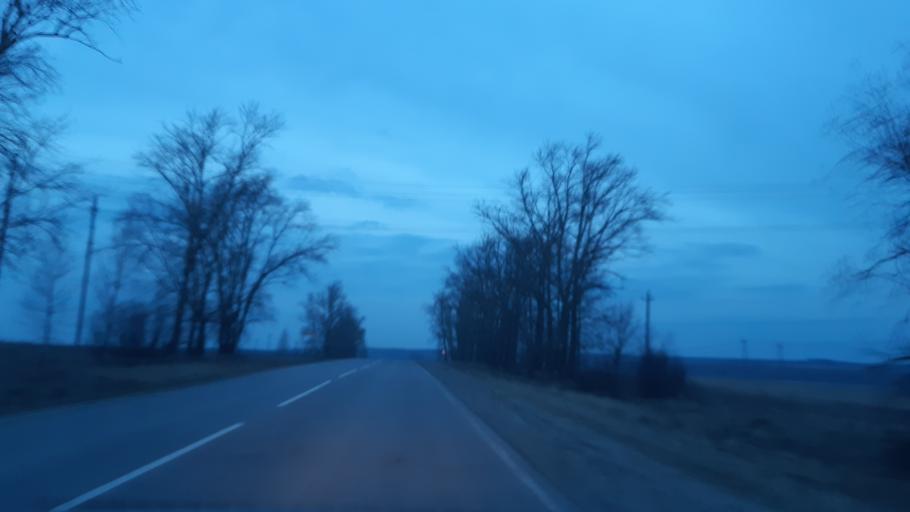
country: RU
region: Vladimir
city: Nikologory
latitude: 56.1632
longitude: 41.9963
